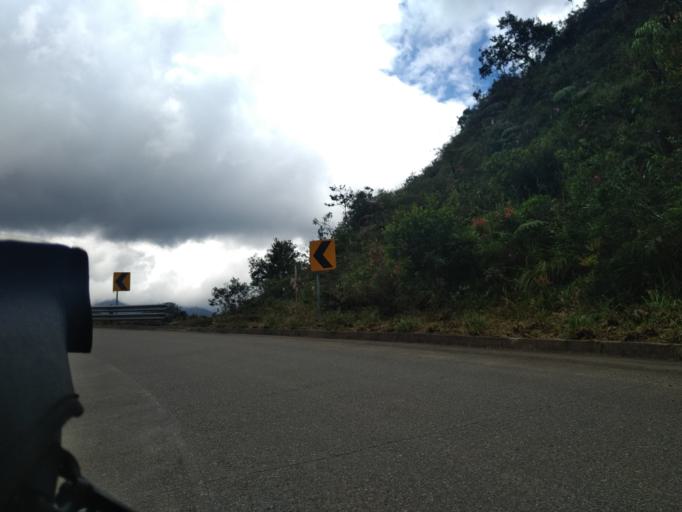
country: EC
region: Zamora-Chinchipe
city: Zamora
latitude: -4.4267
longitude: -79.1492
